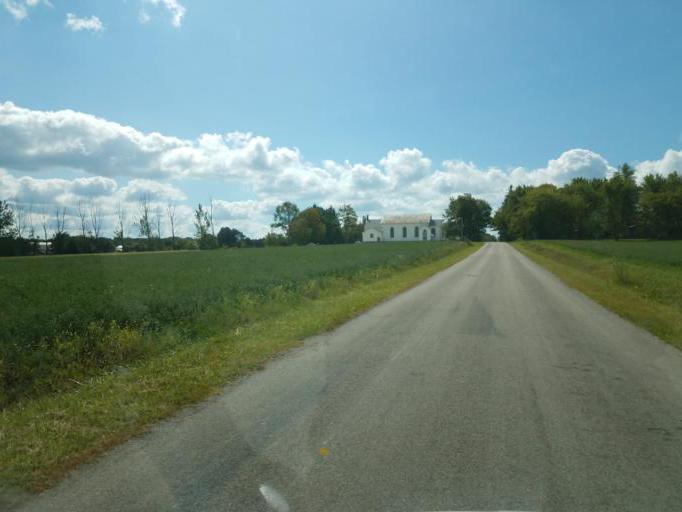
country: US
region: Ohio
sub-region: Wayne County
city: West Salem
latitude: 41.0453
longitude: -82.0963
